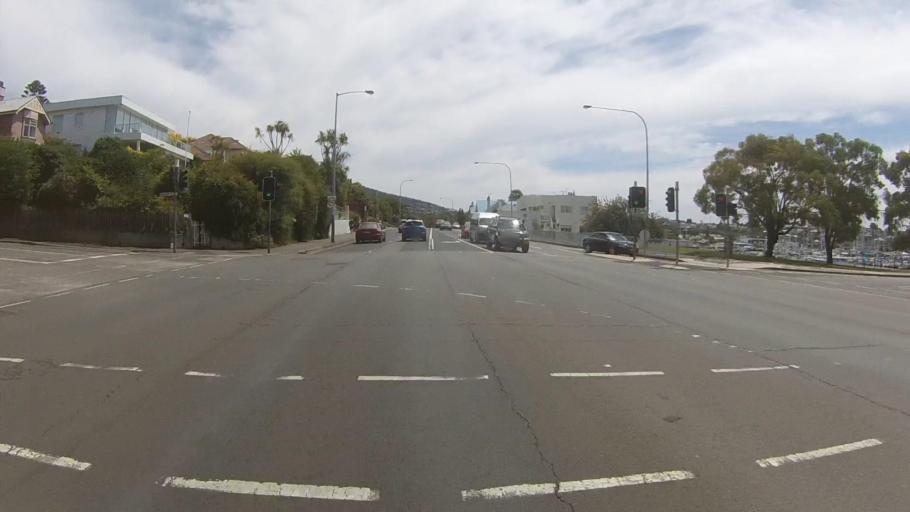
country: AU
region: Tasmania
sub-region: Hobart
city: Sandy Bay
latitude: -42.9020
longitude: 147.3340
